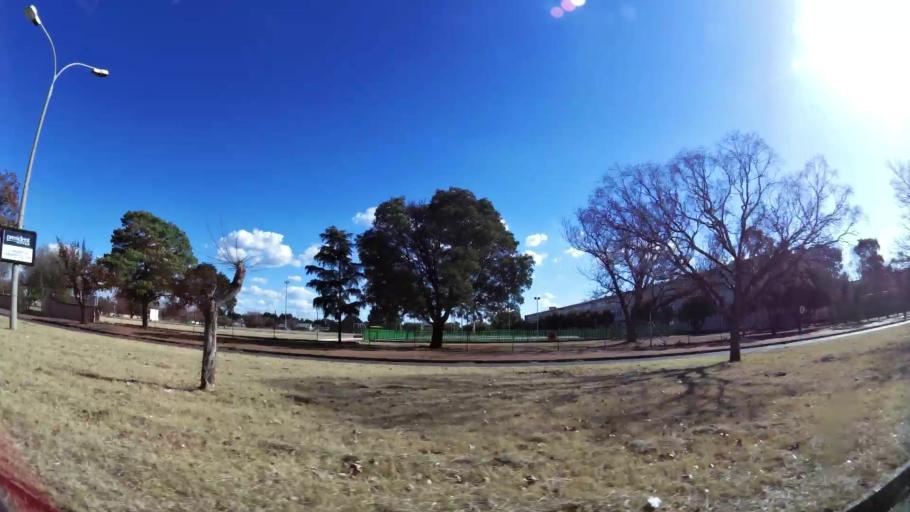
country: ZA
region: Gauteng
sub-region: West Rand District Municipality
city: Carletonville
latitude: -26.3612
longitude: 27.3925
